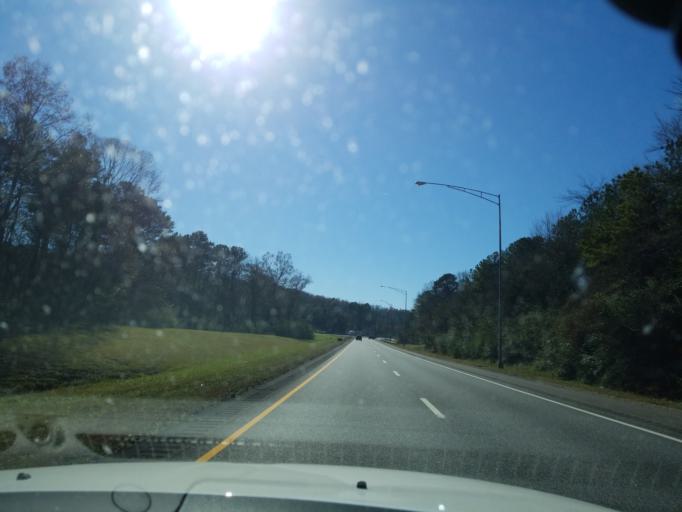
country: US
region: Alabama
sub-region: Jefferson County
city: Bessemer
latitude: 33.3391
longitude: -87.0341
